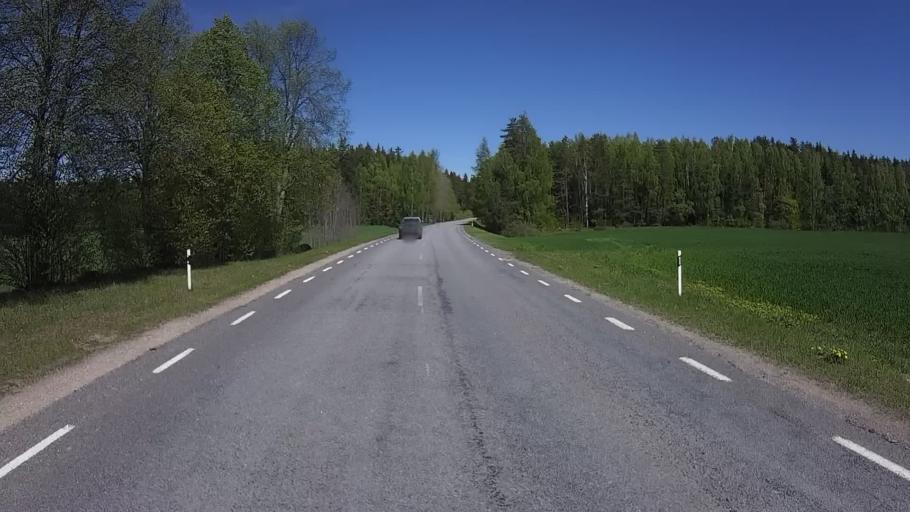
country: EE
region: Polvamaa
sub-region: Raepina vald
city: Rapina
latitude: 58.0514
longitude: 27.3862
